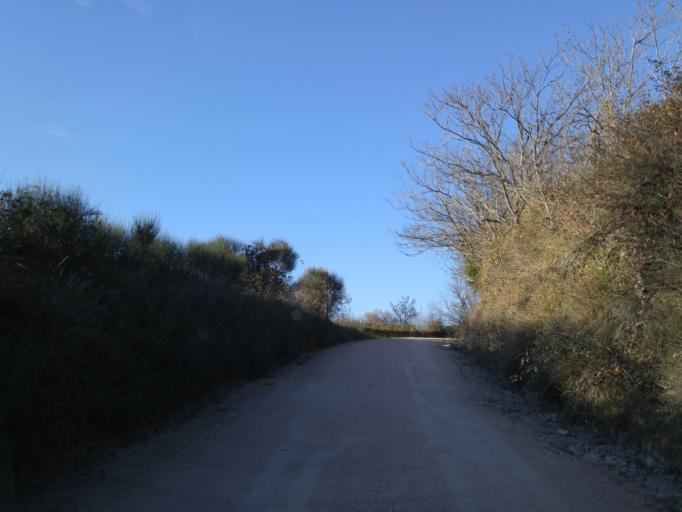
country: IT
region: The Marches
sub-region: Provincia di Pesaro e Urbino
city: Montefelcino
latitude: 43.7704
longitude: 12.8126
